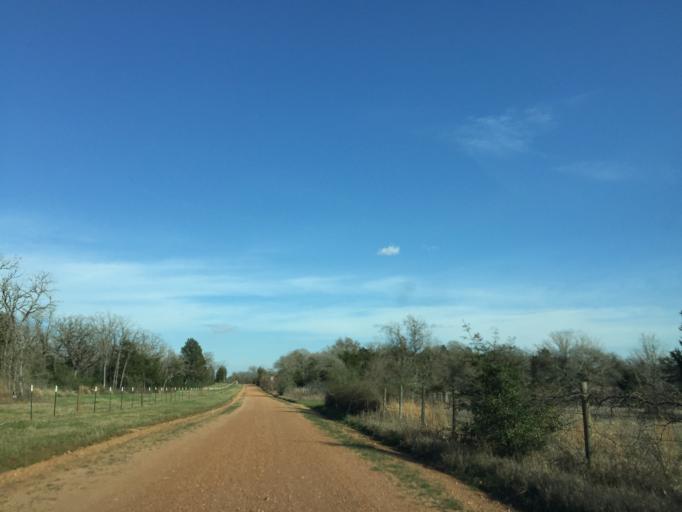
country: US
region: Texas
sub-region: Lee County
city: Lexington
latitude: 30.4458
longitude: -97.1747
